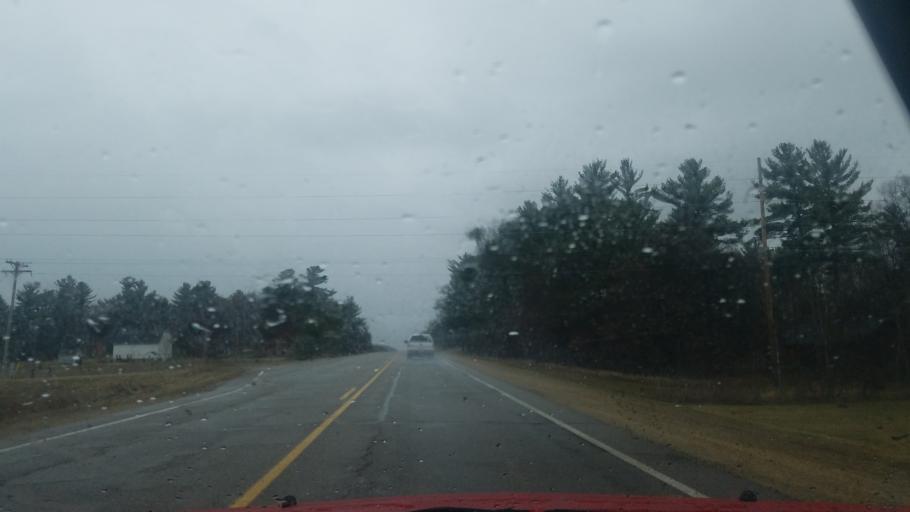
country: US
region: Wisconsin
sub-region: Dunn County
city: Tainter Lake
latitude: 44.9727
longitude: -91.8943
